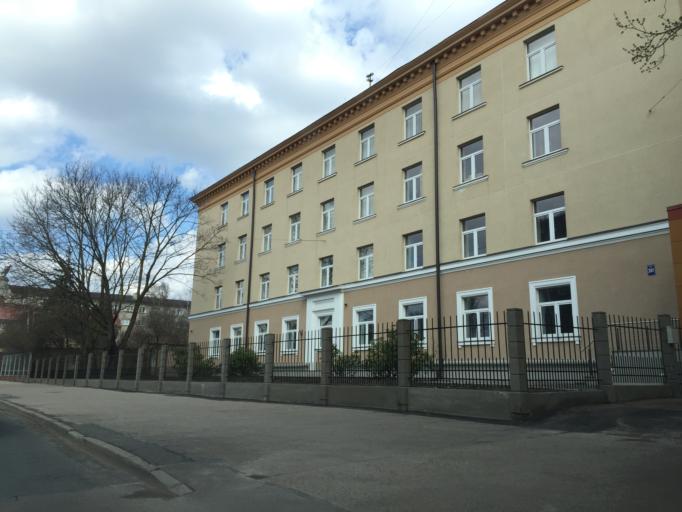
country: LV
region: Riga
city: Riga
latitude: 56.9258
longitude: 24.1680
